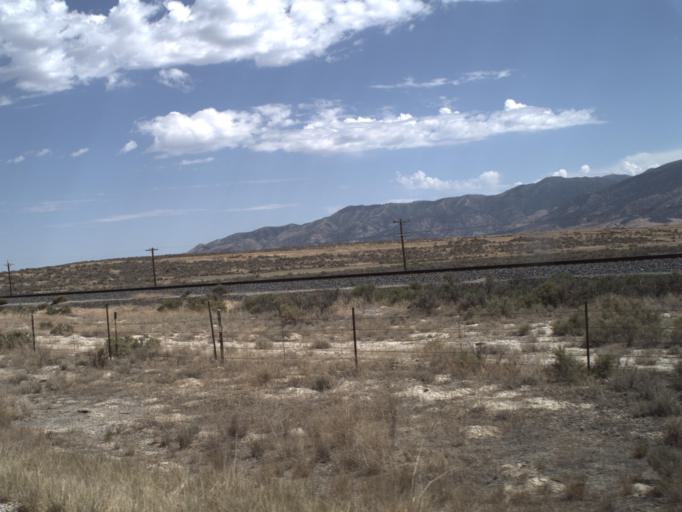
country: US
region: Utah
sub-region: Tooele County
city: Tooele
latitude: 40.3469
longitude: -112.4114
